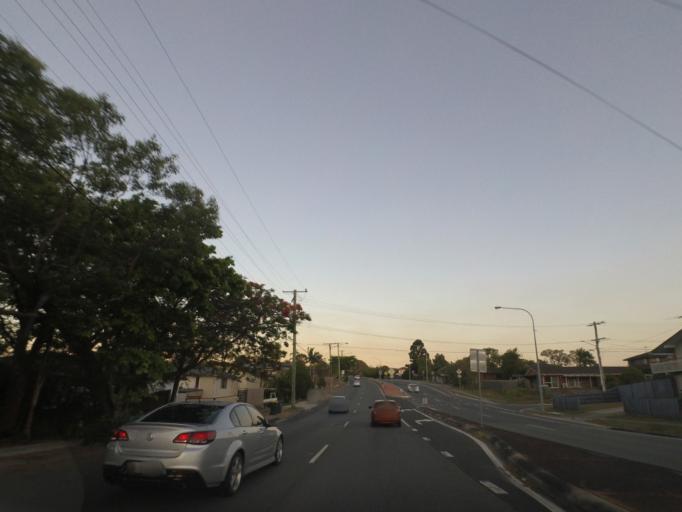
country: AU
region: Queensland
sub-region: Brisbane
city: Upper Mount Gravatt
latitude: -27.5551
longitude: 153.0949
